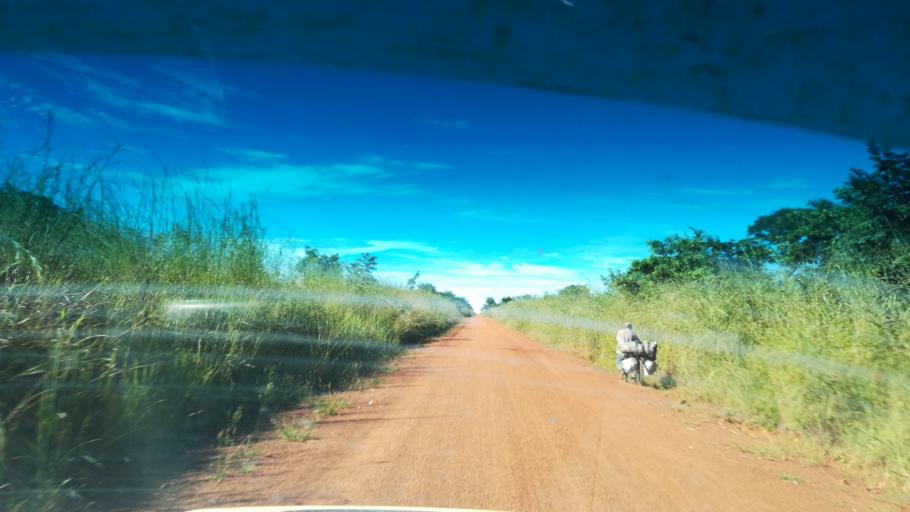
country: ZM
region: Luapula
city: Nchelenge
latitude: -9.3386
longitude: 28.2345
